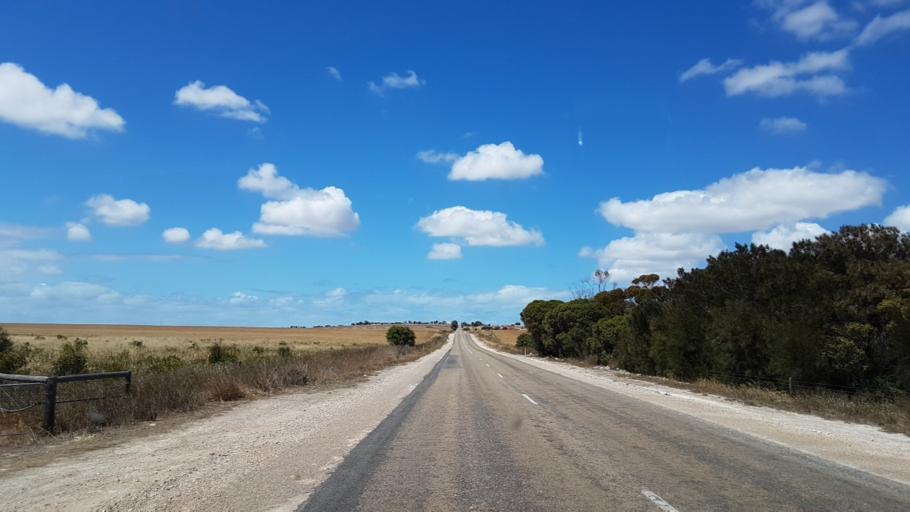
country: AU
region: South Australia
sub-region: Yorke Peninsula
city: Honiton
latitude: -34.9685
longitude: 137.4010
